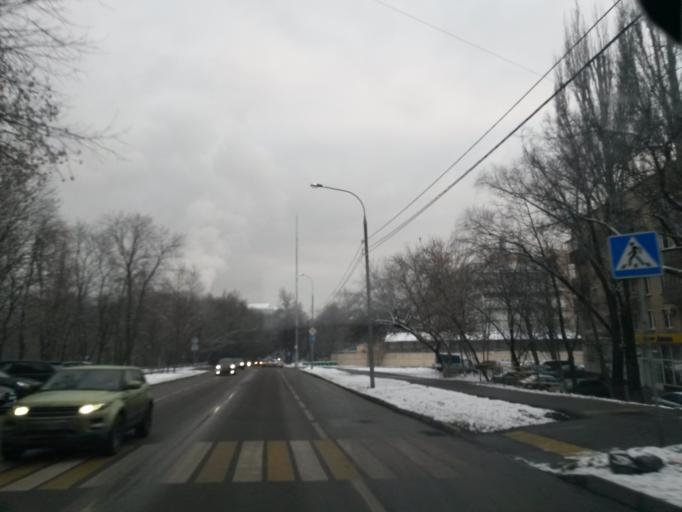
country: RU
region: Moskovskaya
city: Bol'shaya Setun'
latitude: 55.7157
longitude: 37.4375
